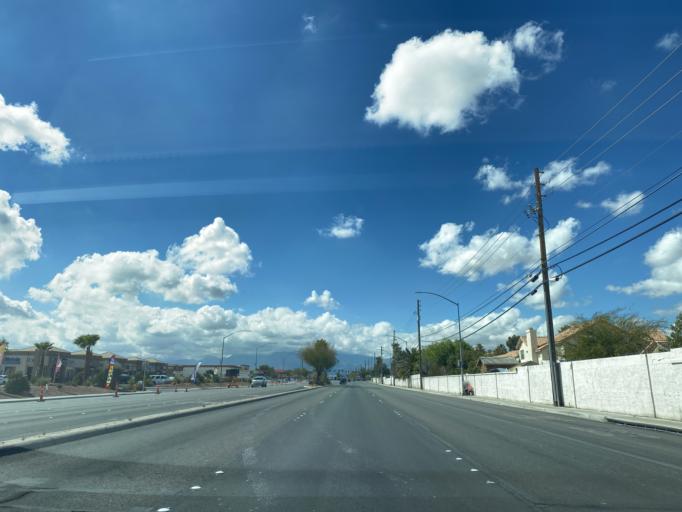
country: US
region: Nevada
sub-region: Clark County
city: North Las Vegas
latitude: 36.2395
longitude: -115.1847
